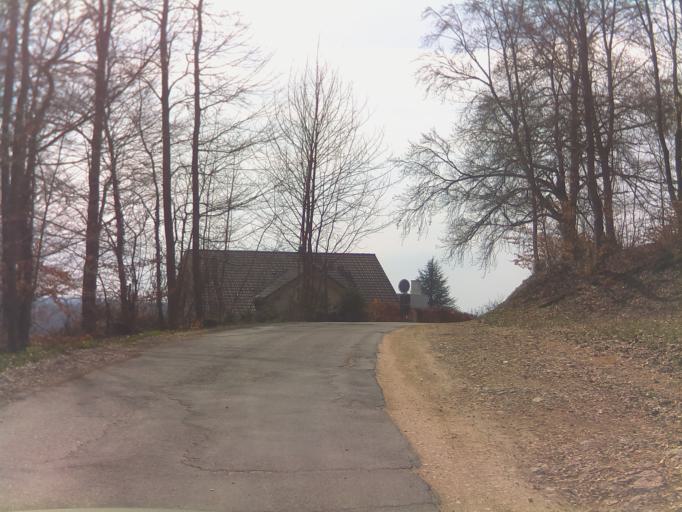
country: DE
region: Baden-Wuerttemberg
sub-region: Tuebingen Region
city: Gomadingen
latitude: 48.4283
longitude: 9.4356
